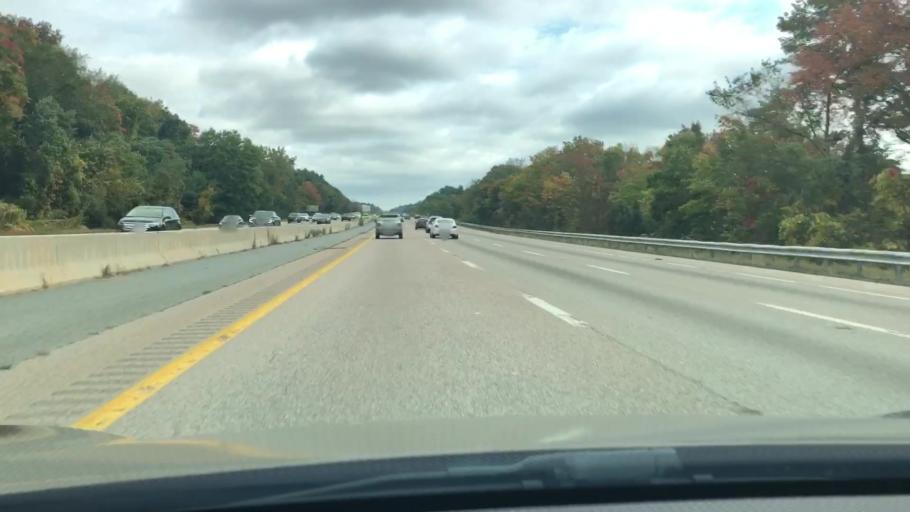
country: US
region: Massachusetts
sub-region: Worcester County
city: Cordaville
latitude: 42.2740
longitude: -71.5412
